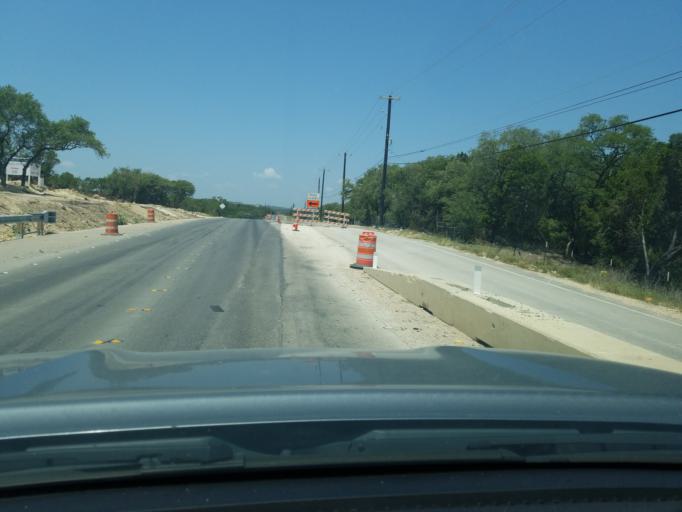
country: US
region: Texas
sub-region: Bexar County
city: Timberwood Park
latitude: 29.7082
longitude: -98.5019
